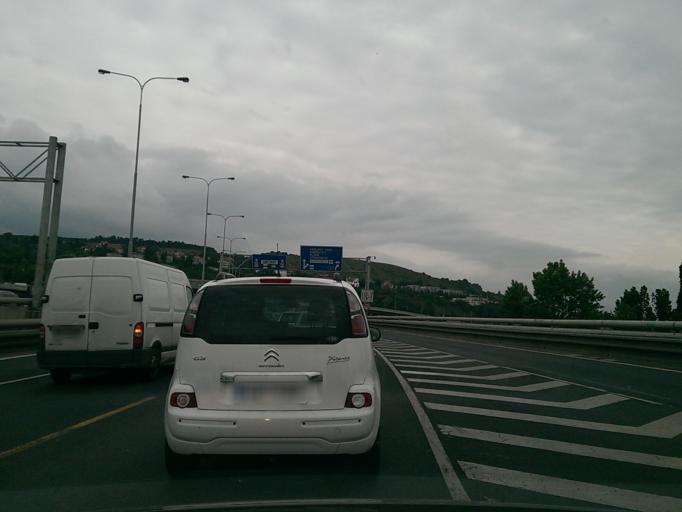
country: CZ
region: Praha
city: Branik
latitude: 50.0378
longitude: 14.4083
